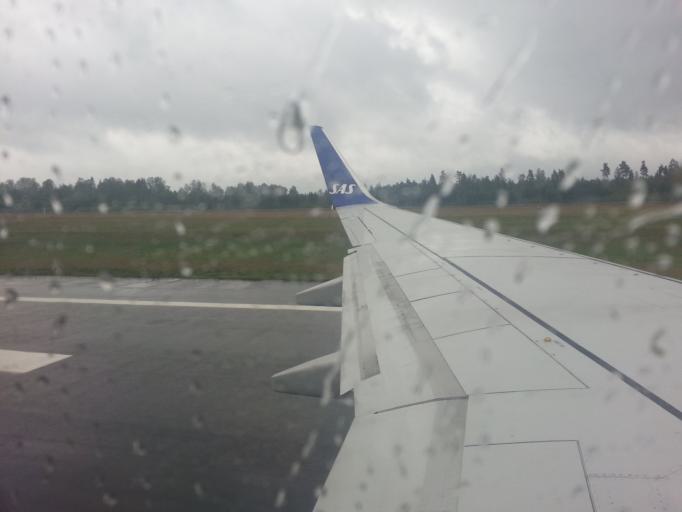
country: NO
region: Akershus
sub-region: Ullensaker
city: Jessheim
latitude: 60.1957
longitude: 11.1192
